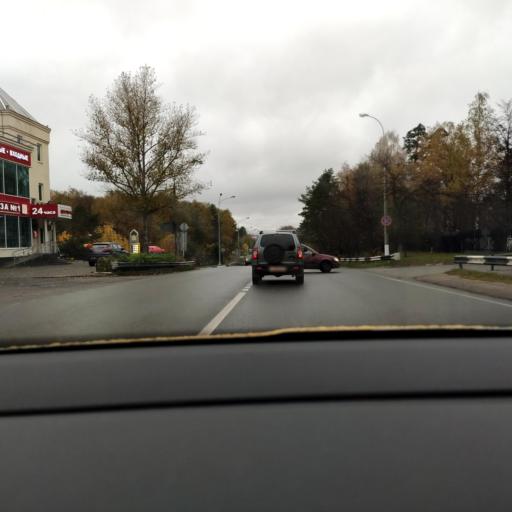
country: RU
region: Moskovskaya
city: Lesnyye Polyany
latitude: 55.9836
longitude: 37.8842
